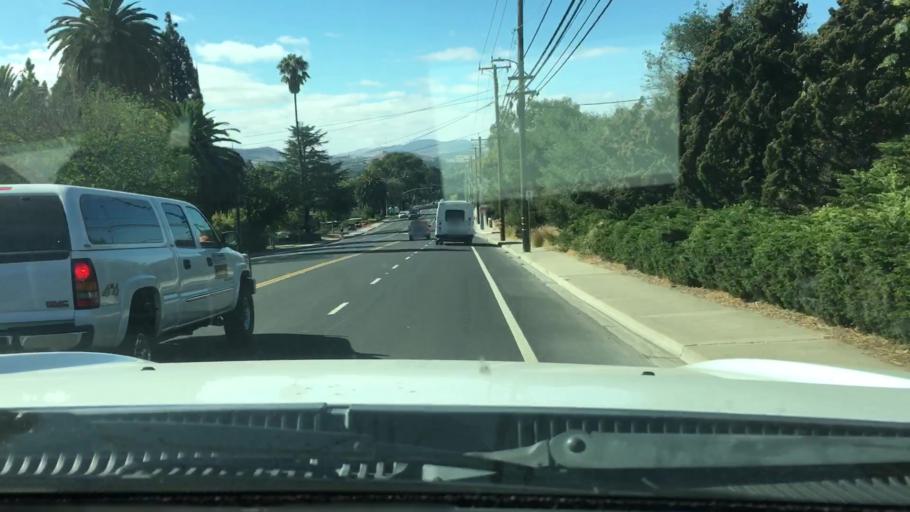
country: US
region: California
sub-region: San Luis Obispo County
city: San Luis Obispo
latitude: 35.2756
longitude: -120.6474
